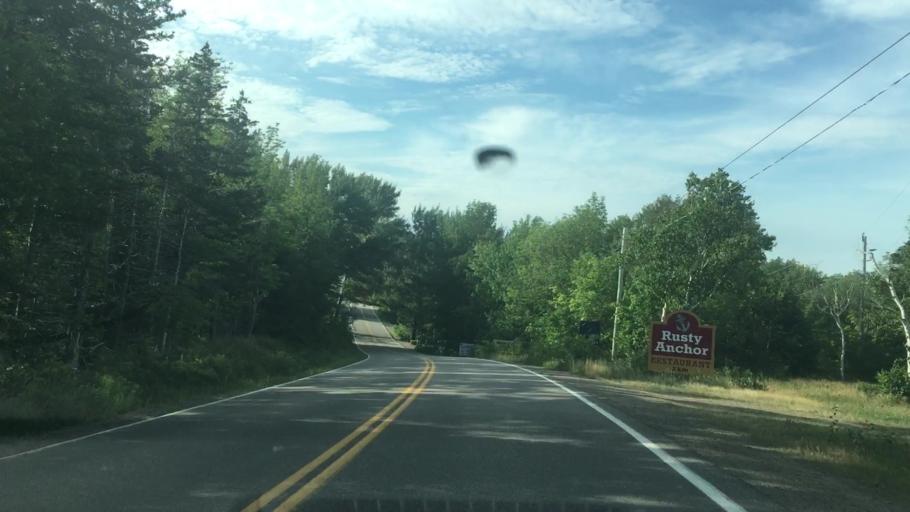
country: CA
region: Nova Scotia
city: Sydney Mines
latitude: 46.8207
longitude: -60.7968
